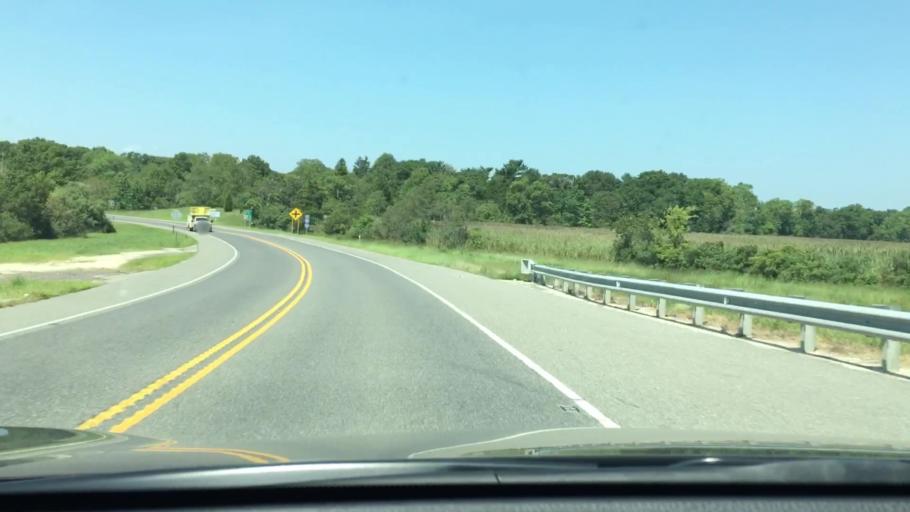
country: US
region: New Jersey
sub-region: Cumberland County
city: Port Norris
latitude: 39.2892
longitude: -74.9916
